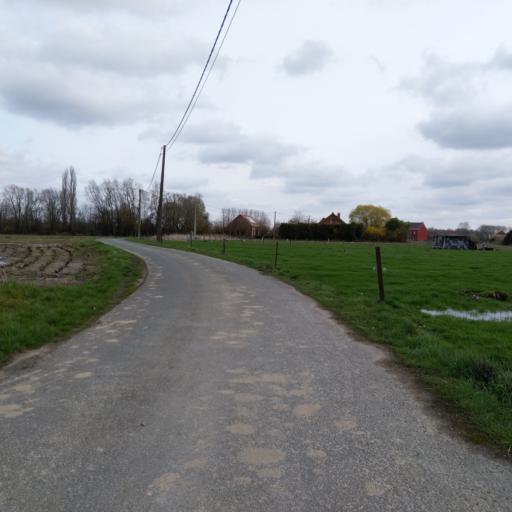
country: BE
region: Wallonia
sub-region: Province du Hainaut
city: Soignies
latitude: 50.5345
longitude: 4.0009
